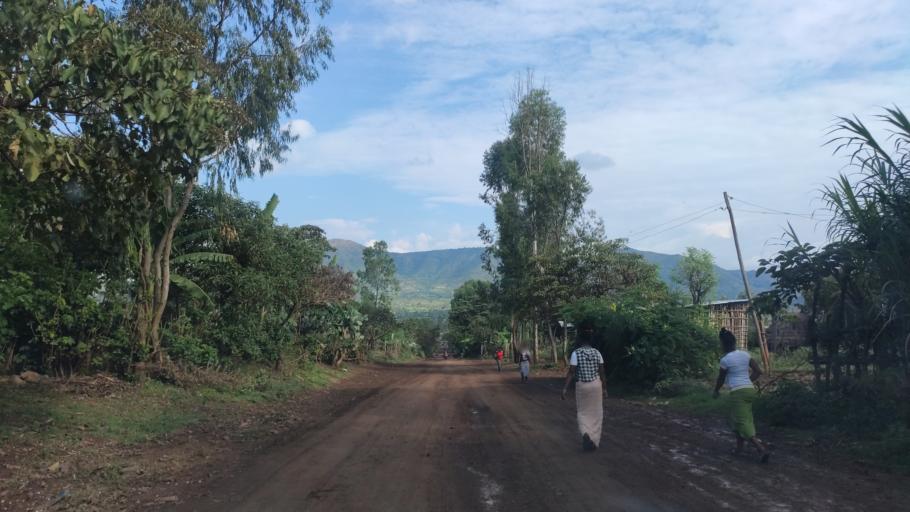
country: ET
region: Southern Nations, Nationalities, and People's Region
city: Felege Neway
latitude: 6.4271
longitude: 37.3048
